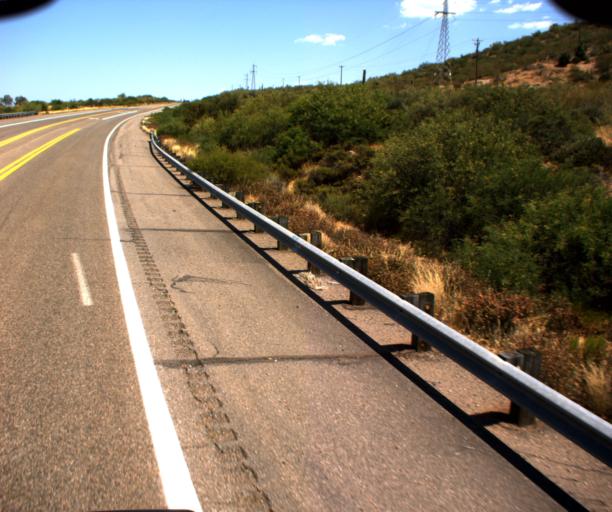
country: US
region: Arizona
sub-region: Gila County
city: Tonto Basin
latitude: 33.6638
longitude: -111.1219
